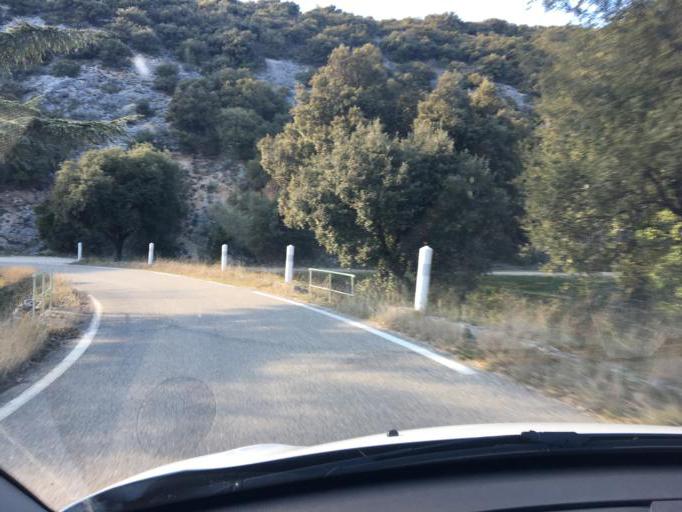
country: FR
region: Provence-Alpes-Cote d'Azur
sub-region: Departement du Vaucluse
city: Villes-sur-Auzon
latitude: 44.0581
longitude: 5.2488
